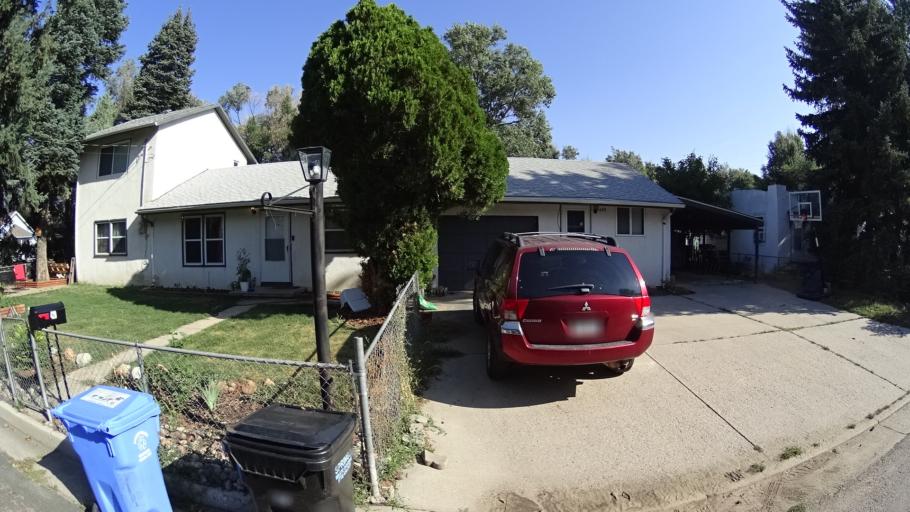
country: US
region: Colorado
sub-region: El Paso County
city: Colorado Springs
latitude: 38.8689
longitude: -104.8292
